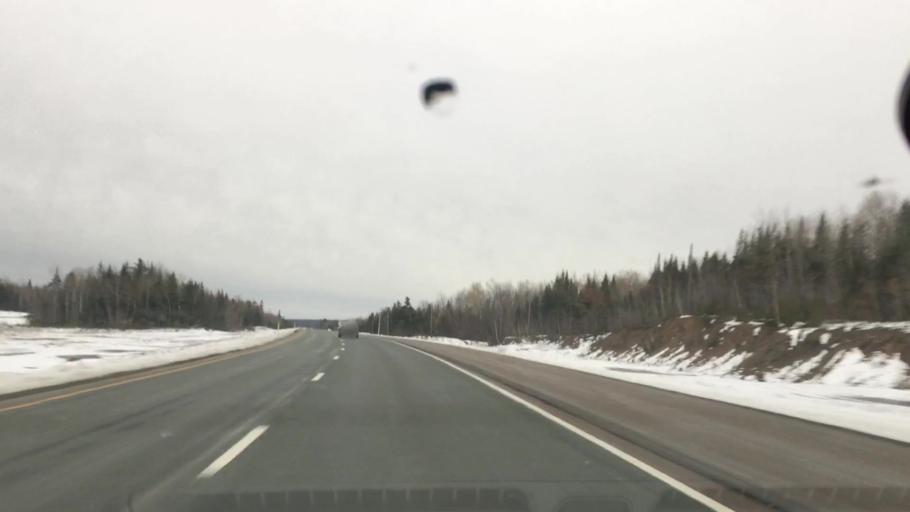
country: CA
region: New Brunswick
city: Fredericton
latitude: 45.9269
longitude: -66.7664
